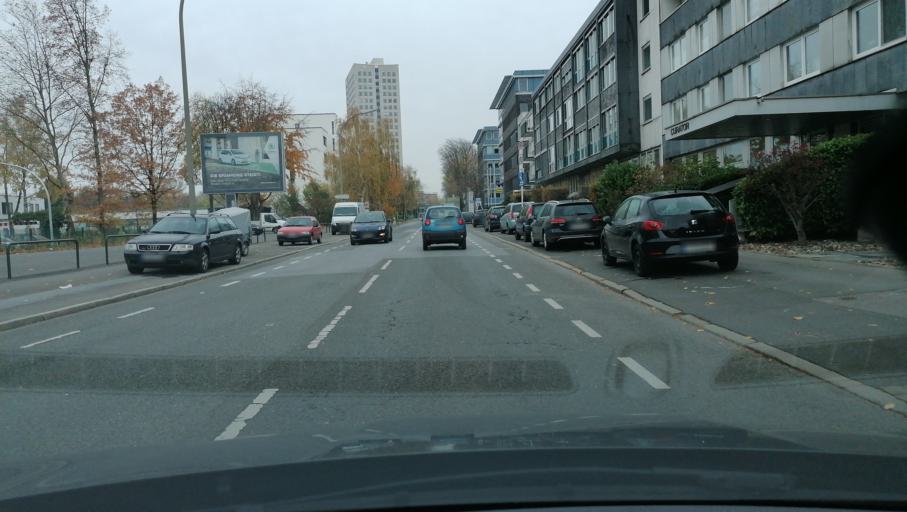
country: DE
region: North Rhine-Westphalia
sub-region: Regierungsbezirk Arnsberg
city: Dortmund
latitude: 51.4995
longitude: 7.4970
